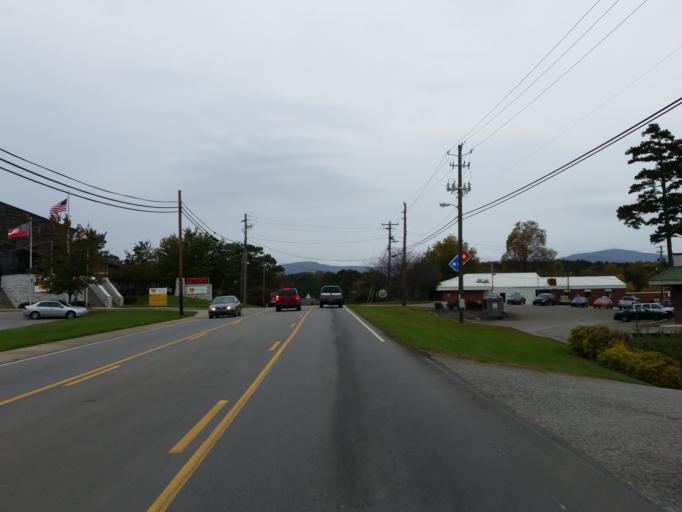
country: US
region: Georgia
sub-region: Pickens County
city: Jasper
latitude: 34.4698
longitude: -84.4263
